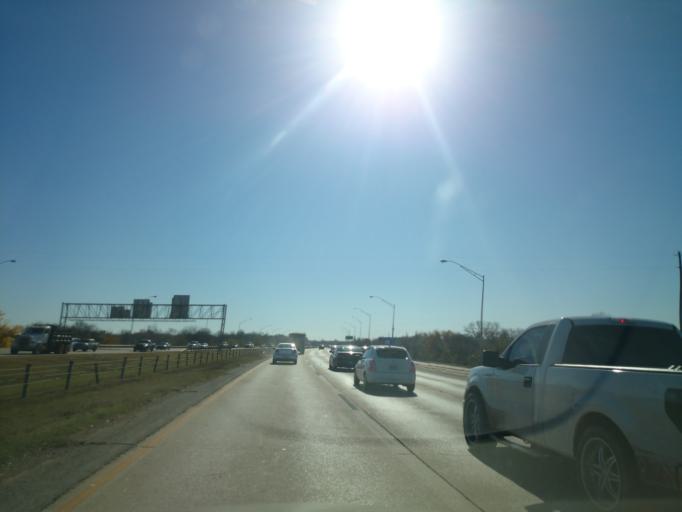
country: US
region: Oklahoma
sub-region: Oklahoma County
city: Oklahoma City
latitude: 35.4474
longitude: -97.5702
